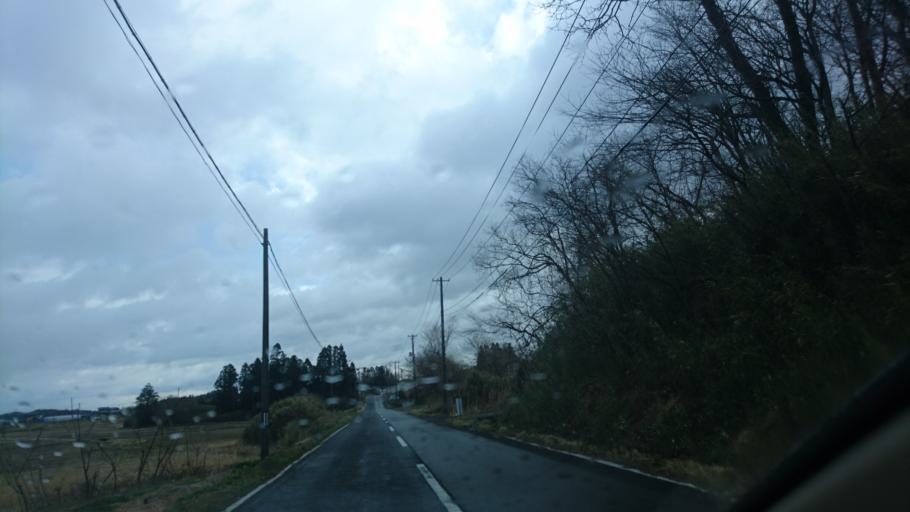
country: JP
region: Iwate
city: Ichinoseki
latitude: 38.7620
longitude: 141.0305
